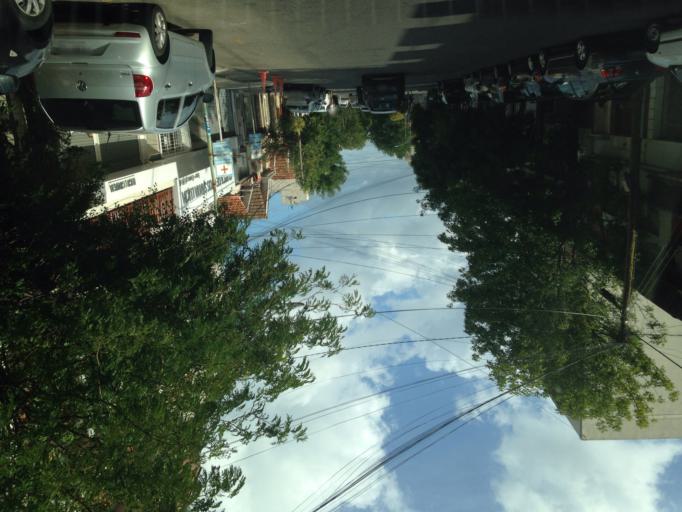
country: AR
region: Buenos Aires
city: Mar del Plata
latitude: -37.9936
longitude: -57.5536
